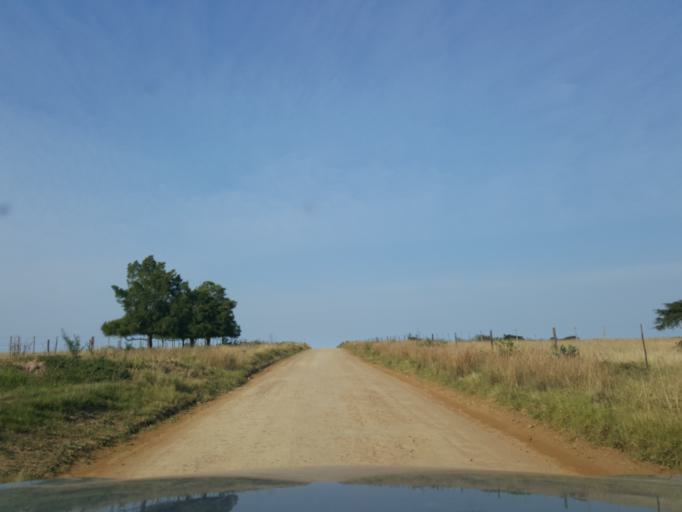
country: ZA
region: Eastern Cape
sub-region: Cacadu District Municipality
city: Grahamstown
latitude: -33.4239
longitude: 26.3188
